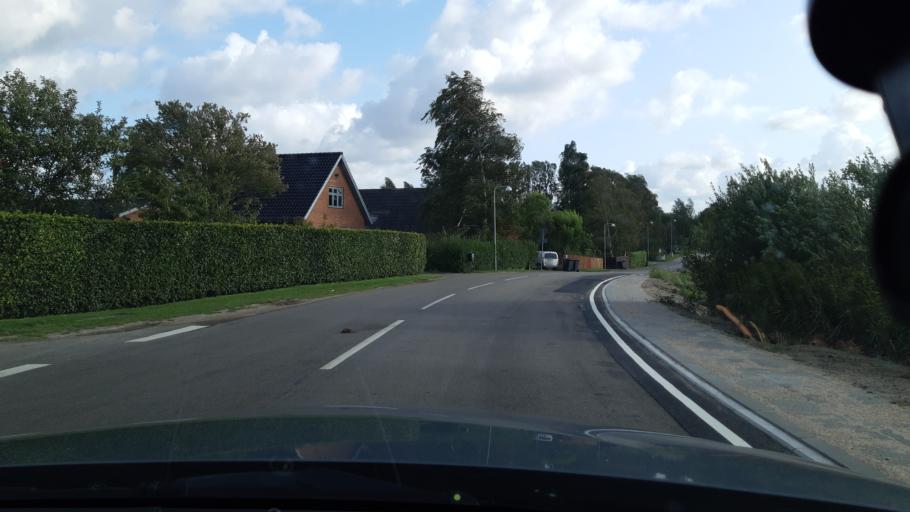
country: DK
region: Zealand
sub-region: Holbaek Kommune
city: Holbaek
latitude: 55.6563
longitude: 11.6473
